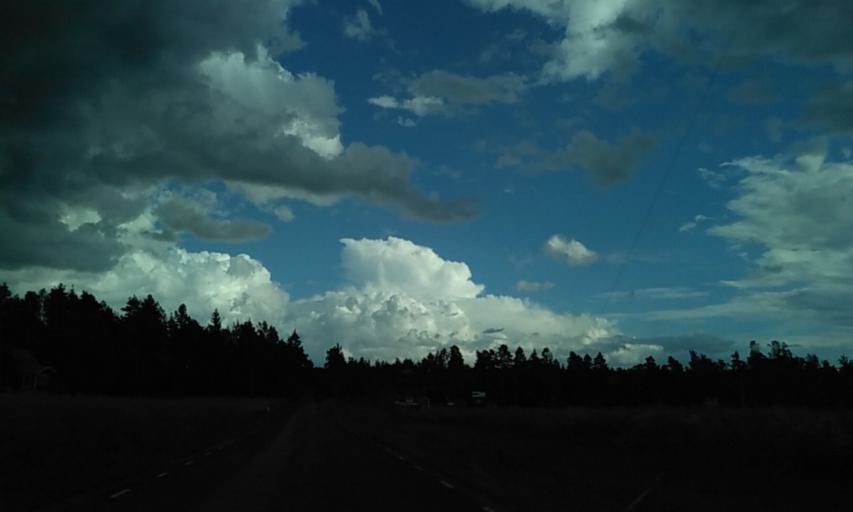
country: SE
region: Vaestra Goetaland
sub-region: Lidkopings Kommun
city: Lidkoping
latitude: 58.5154
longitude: 12.9933
